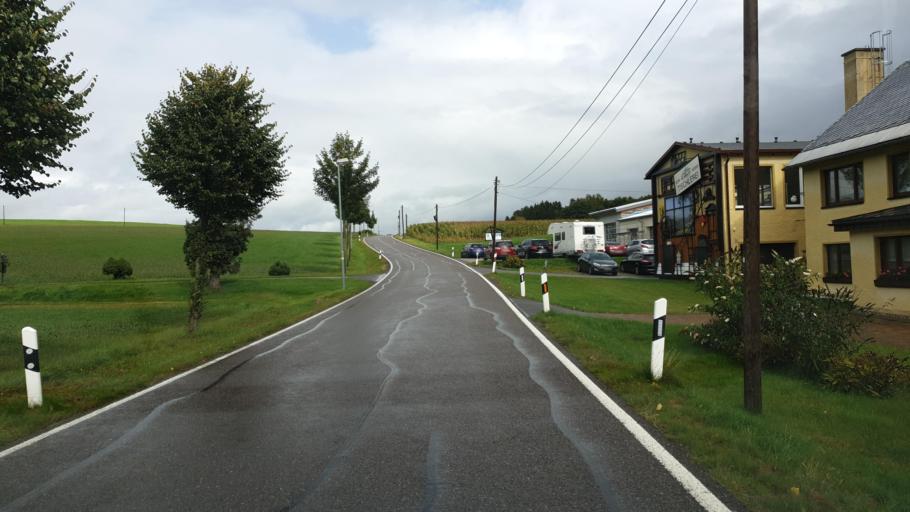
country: DE
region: Saxony
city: Neuhausen
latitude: 50.6995
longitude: 13.4865
